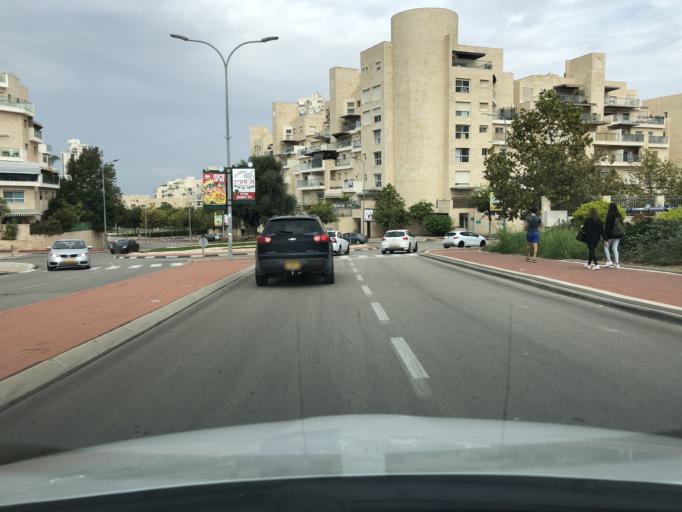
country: IL
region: Central District
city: Modiin
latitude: 31.9101
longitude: 35.0135
